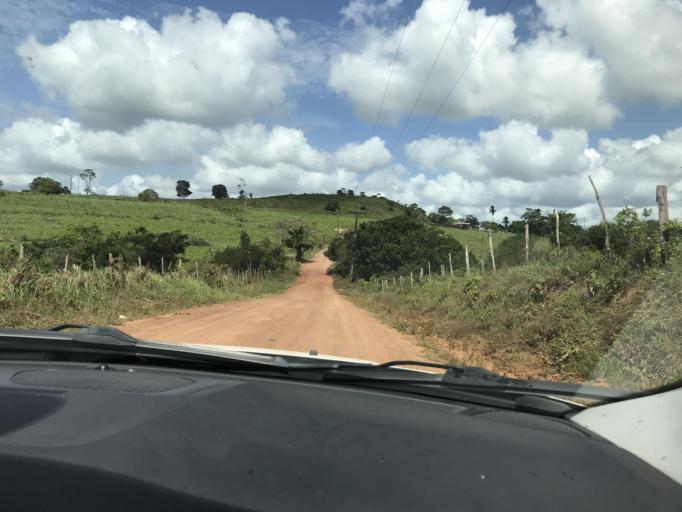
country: BR
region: Bahia
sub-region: Entre Rios
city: Entre Rios
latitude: -12.1844
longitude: -38.0551
